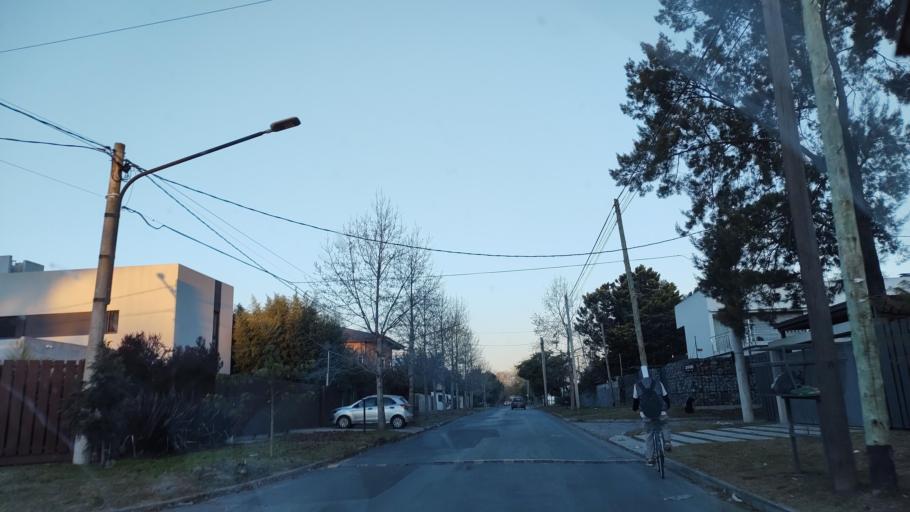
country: AR
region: Buenos Aires
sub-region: Partido de La Plata
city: La Plata
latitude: -34.9042
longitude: -58.0265
